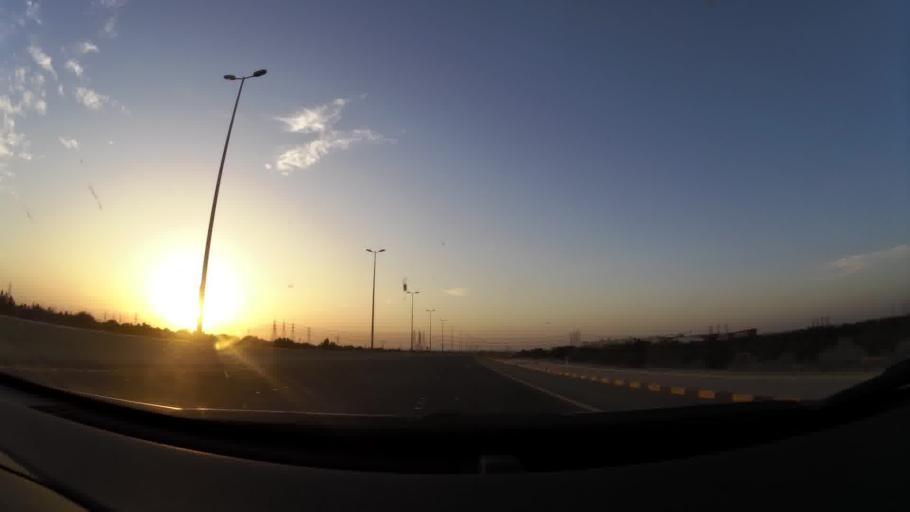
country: KW
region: Muhafazat al Jahra'
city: Al Jahra'
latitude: 29.3194
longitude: 47.7944
